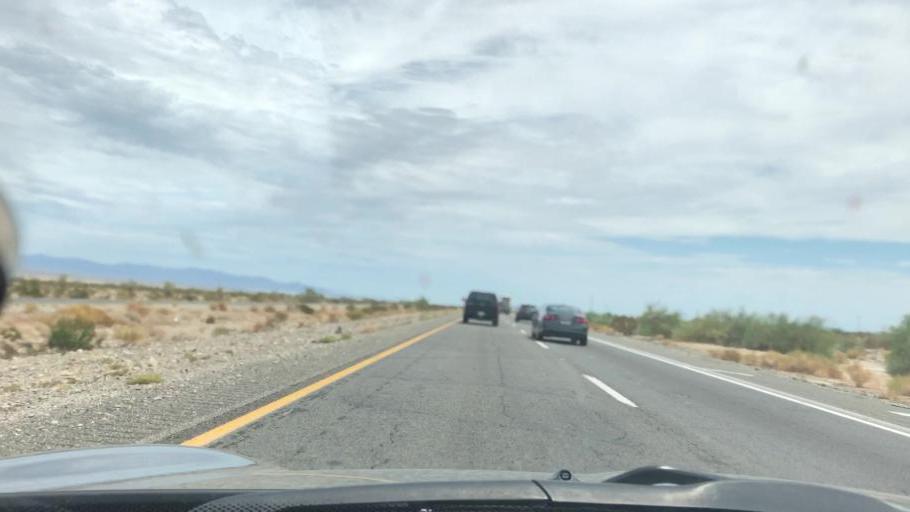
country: US
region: California
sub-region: Imperial County
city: Niland
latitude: 33.6891
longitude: -115.2665
